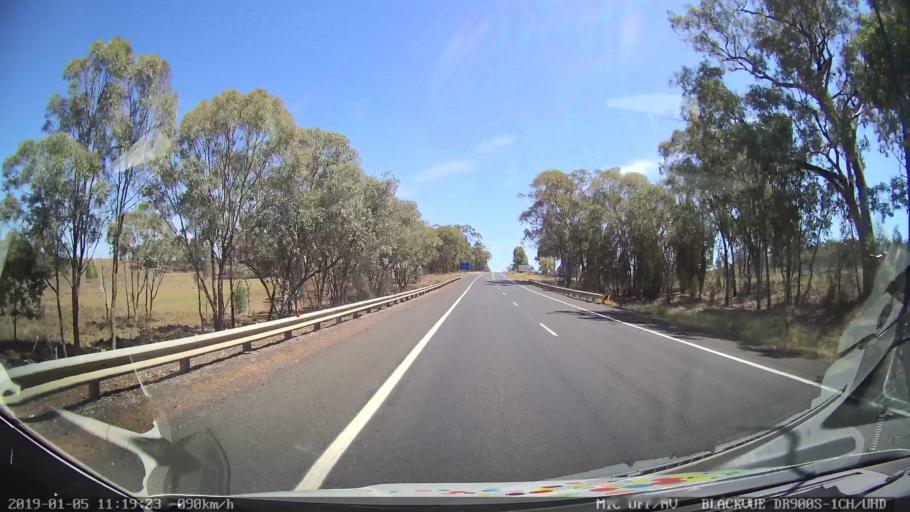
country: AU
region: New South Wales
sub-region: Warrumbungle Shire
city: Coonabarabran
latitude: -31.3046
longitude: 149.2959
